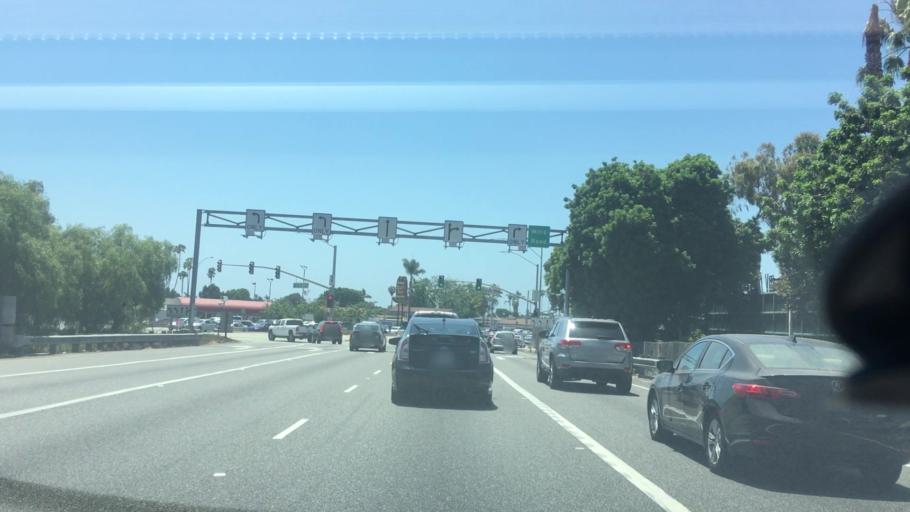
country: US
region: California
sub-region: Ventura County
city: Ventura
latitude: 34.2650
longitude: -119.2435
